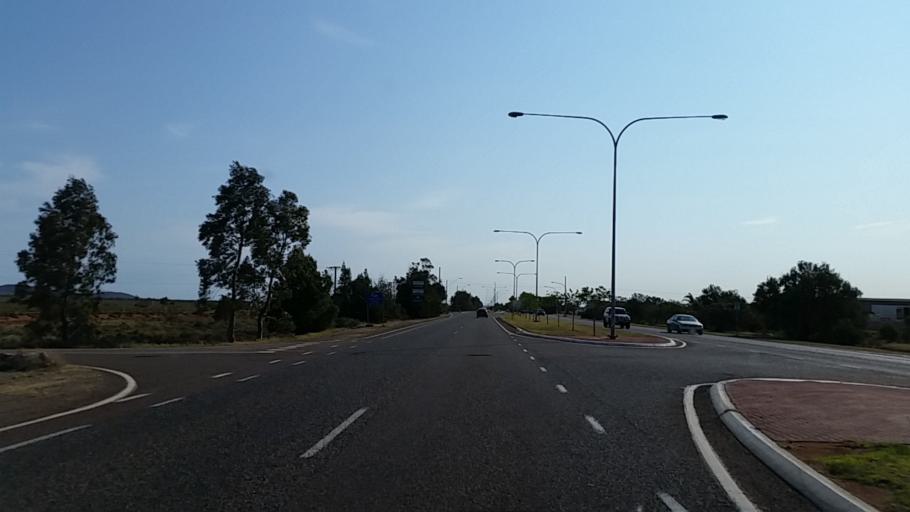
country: AU
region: South Australia
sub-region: Whyalla
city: Whyalla
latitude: -33.0418
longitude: 137.5465
